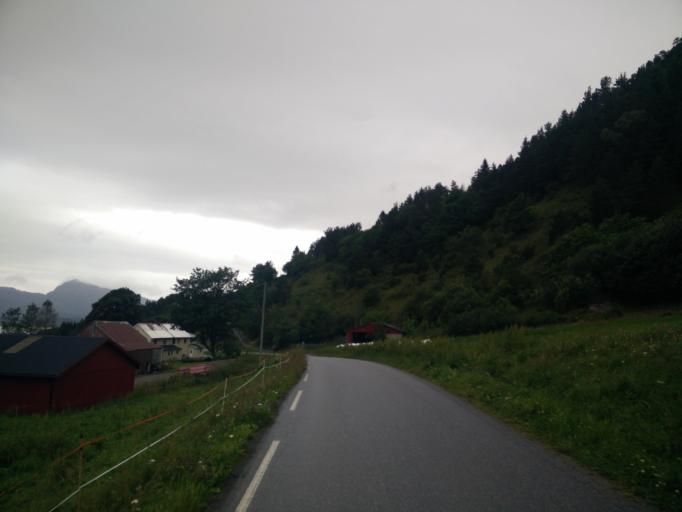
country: NO
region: More og Romsdal
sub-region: Kristiansund
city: Rensvik
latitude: 63.0153
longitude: 7.9111
